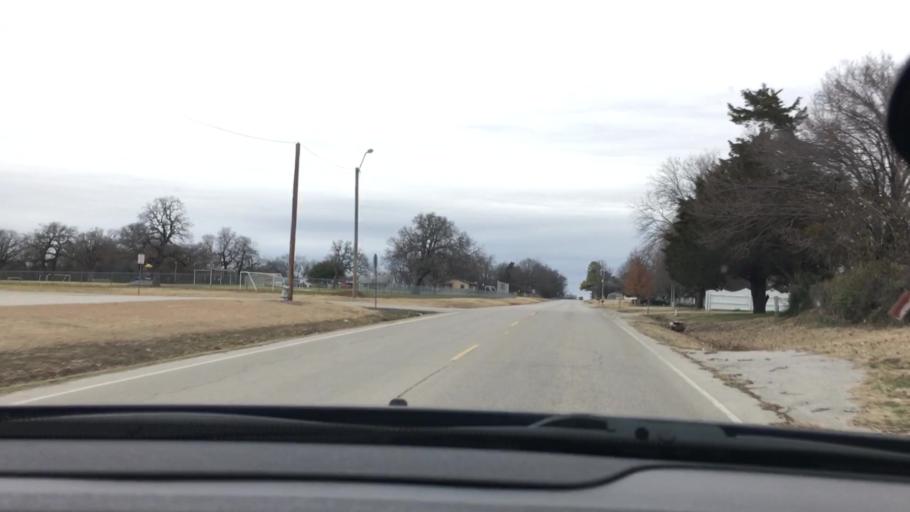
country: US
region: Oklahoma
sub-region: Carter County
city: Ardmore
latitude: 34.1707
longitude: -97.1081
